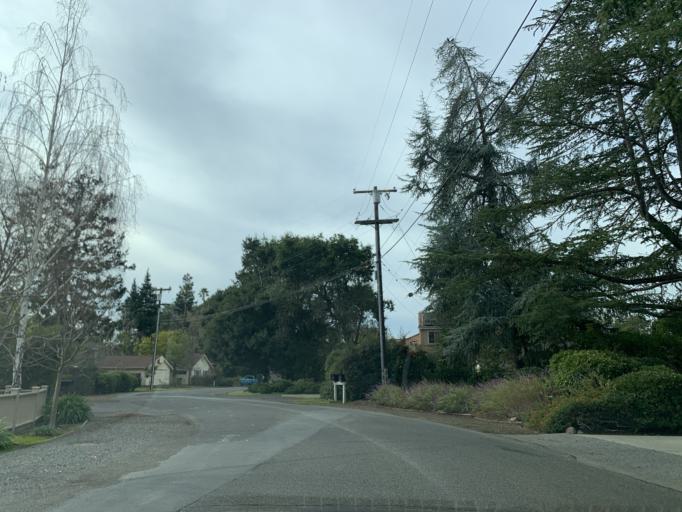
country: US
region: California
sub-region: Santa Clara County
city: Los Altos
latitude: 37.3782
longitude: -122.0993
